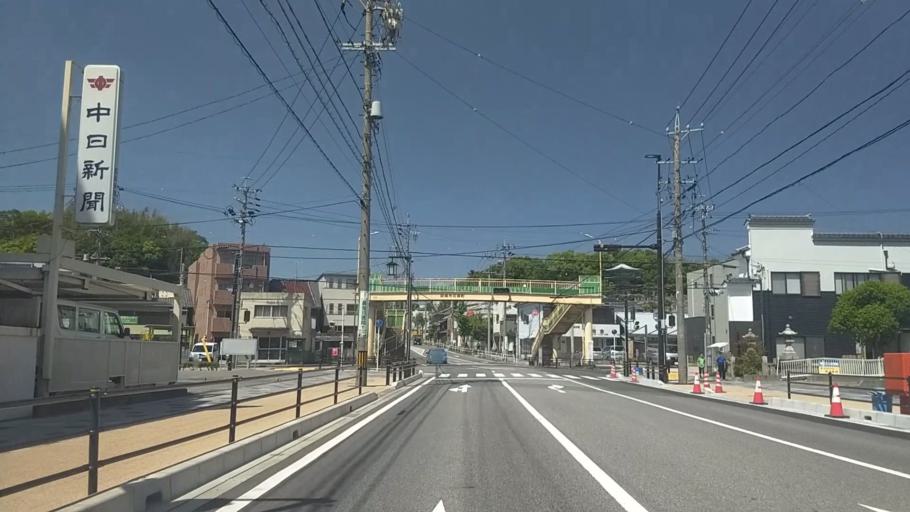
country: JP
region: Aichi
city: Okazaki
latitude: 34.9581
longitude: 137.1708
